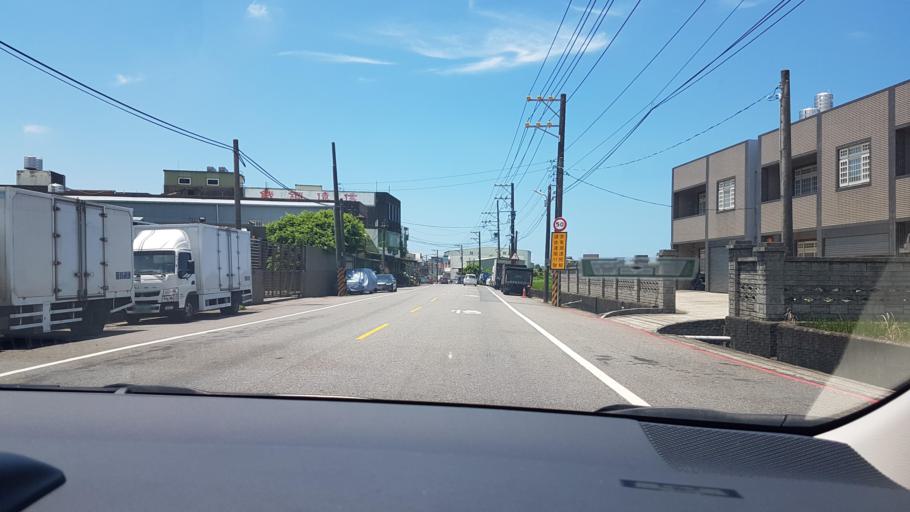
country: TW
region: Taiwan
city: Taoyuan City
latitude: 25.0863
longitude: 121.2845
